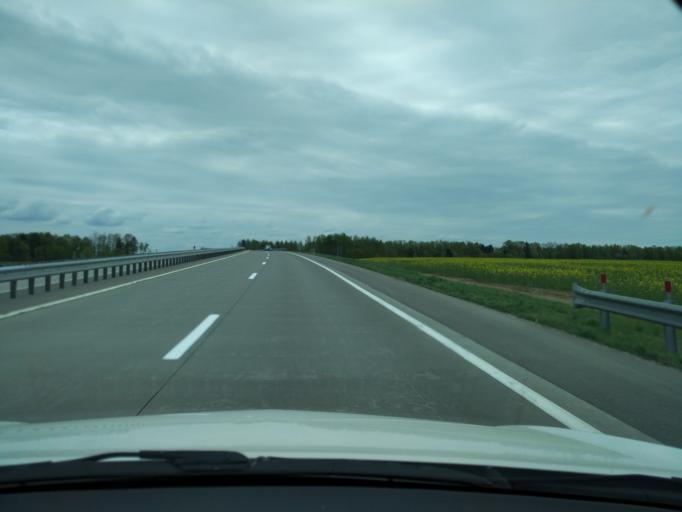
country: BY
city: Fanipol
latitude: 53.7697
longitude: 27.3638
